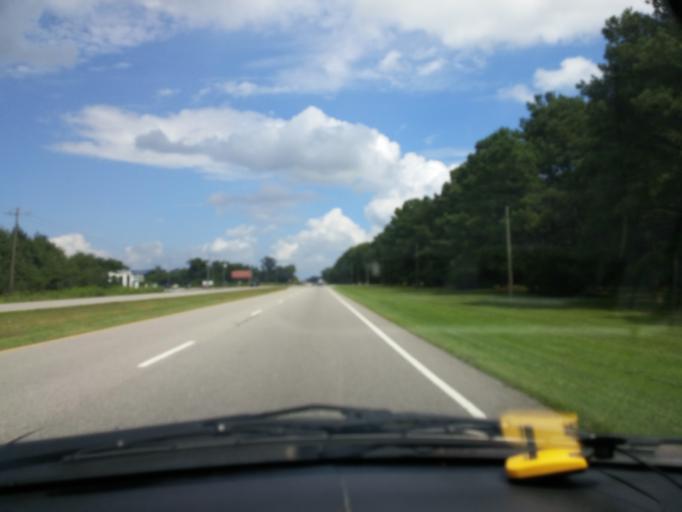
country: US
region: North Carolina
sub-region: Pitt County
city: Grifton
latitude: 35.3368
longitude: -77.4823
